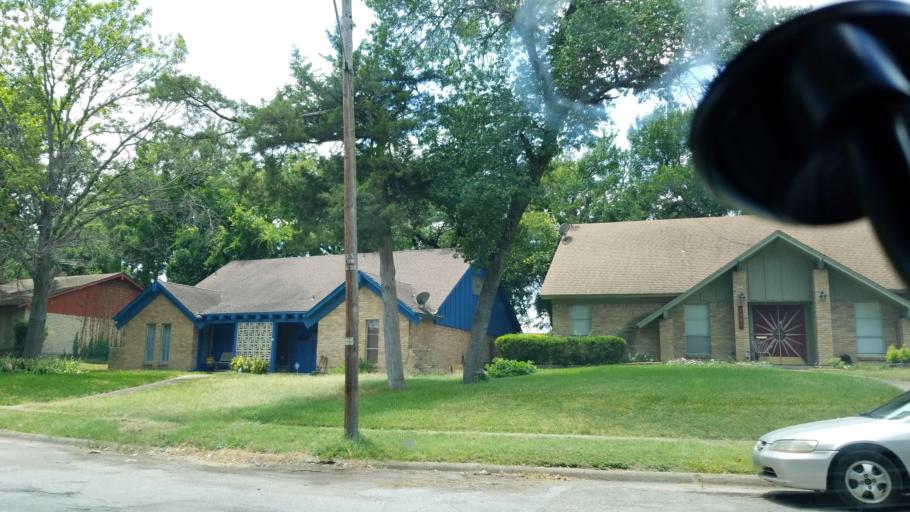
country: US
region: Texas
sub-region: Dallas County
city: Cockrell Hill
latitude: 32.6968
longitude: -96.8486
